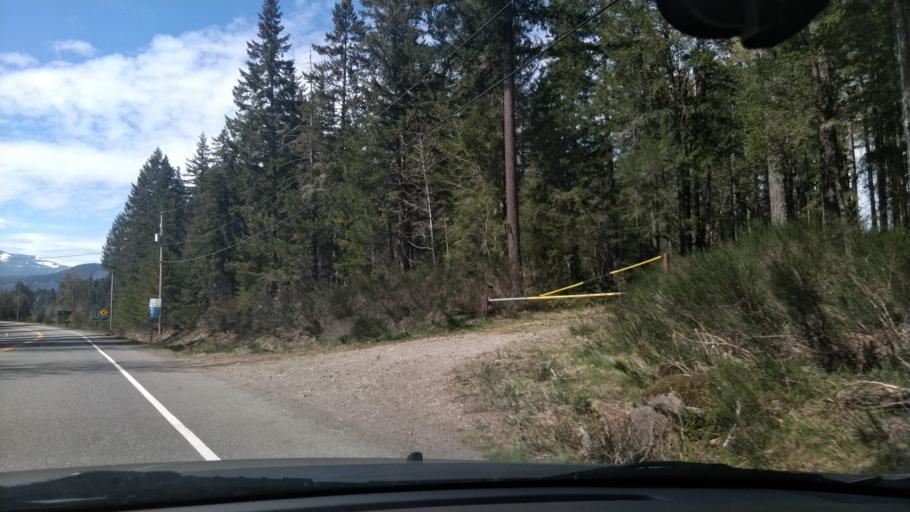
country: CA
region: British Columbia
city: Courtenay
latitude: 49.6961
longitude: -125.0641
